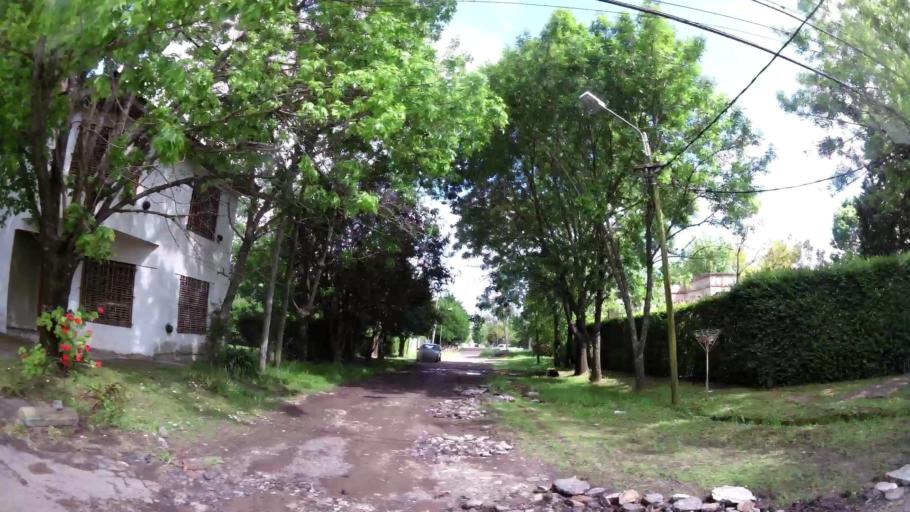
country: AR
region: Buenos Aires
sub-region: Partido de Quilmes
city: Quilmes
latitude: -34.8361
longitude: -58.1689
